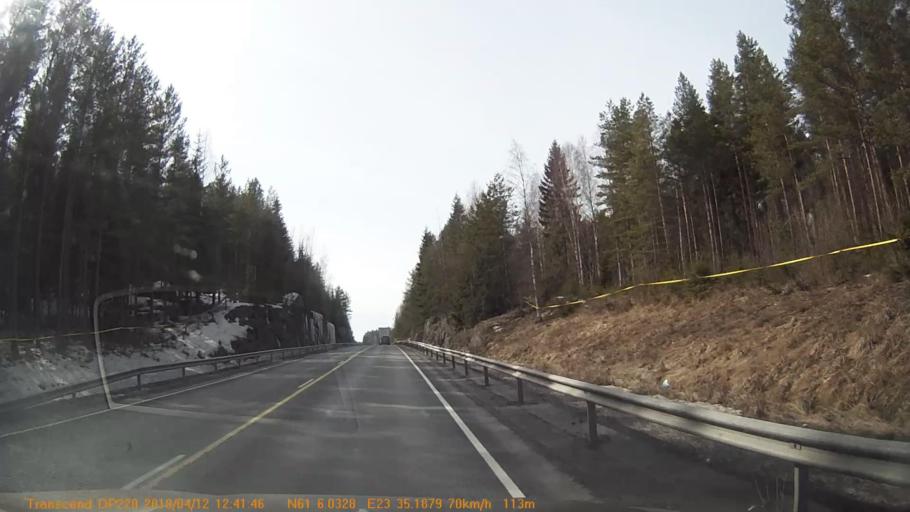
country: FI
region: Pirkanmaa
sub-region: Etelae-Pirkanmaa
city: Urjala
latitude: 61.1005
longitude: 23.5863
